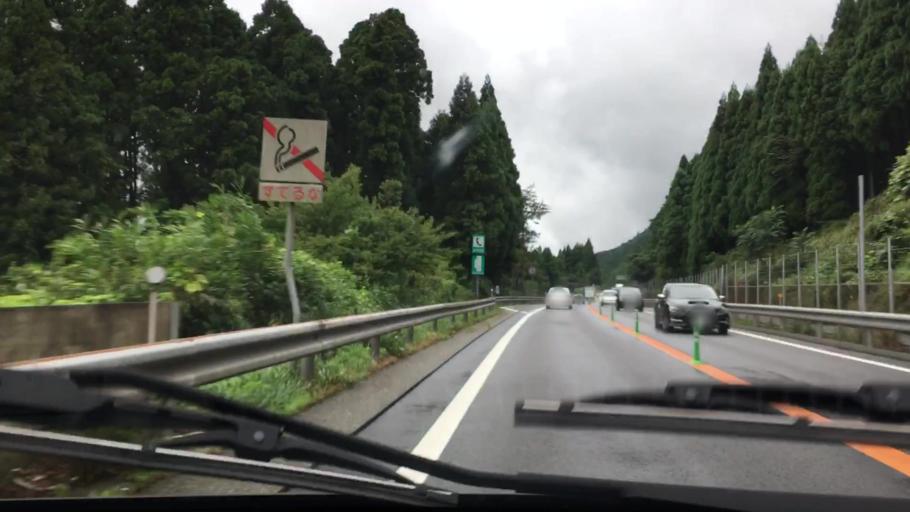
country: JP
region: Hyogo
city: Nishiwaki
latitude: 35.1132
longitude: 134.7833
